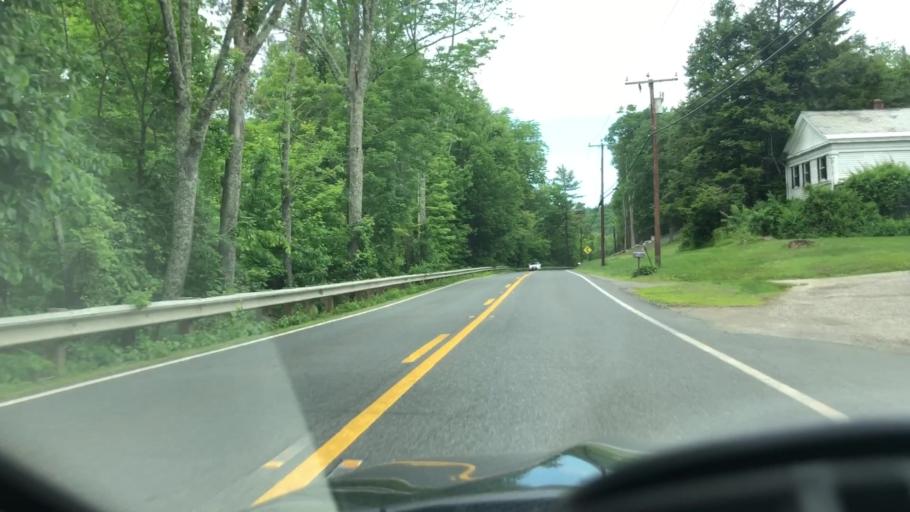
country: US
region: Massachusetts
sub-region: Hampshire County
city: Westhampton
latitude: 42.2539
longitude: -72.8670
